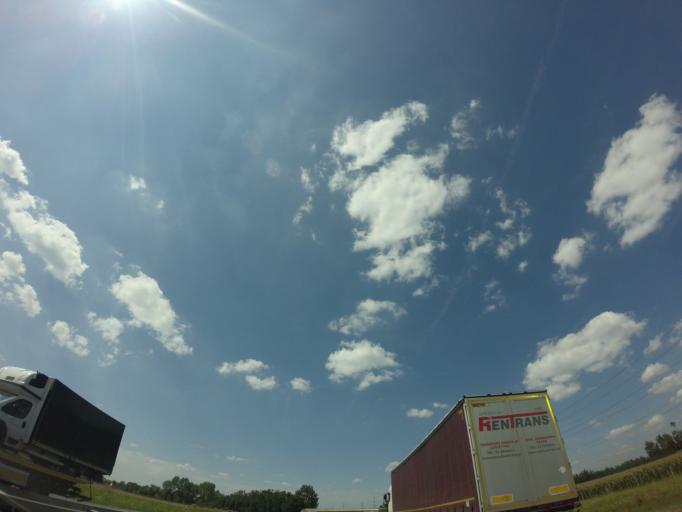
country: PL
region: Lower Silesian Voivodeship
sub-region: Powiat olawski
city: Wierzbno
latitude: 50.8876
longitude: 17.1910
